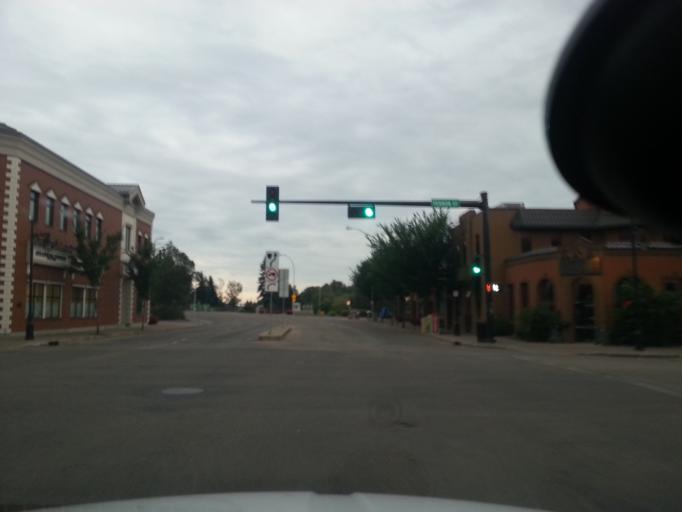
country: CA
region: Alberta
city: St. Albert
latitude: 53.6348
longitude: -113.6260
